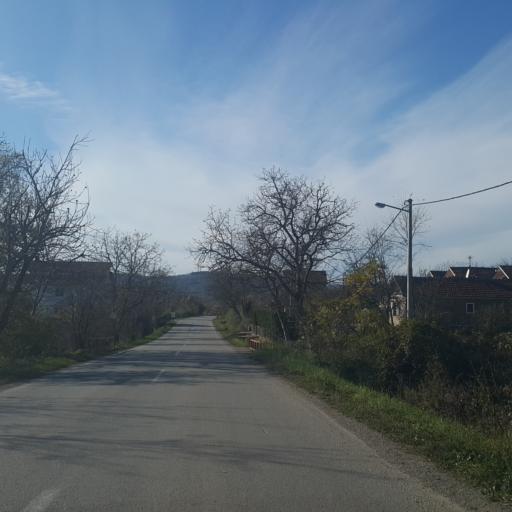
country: RS
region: Central Serbia
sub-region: Sumadijski Okrug
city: Topola
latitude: 44.2500
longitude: 20.7247
